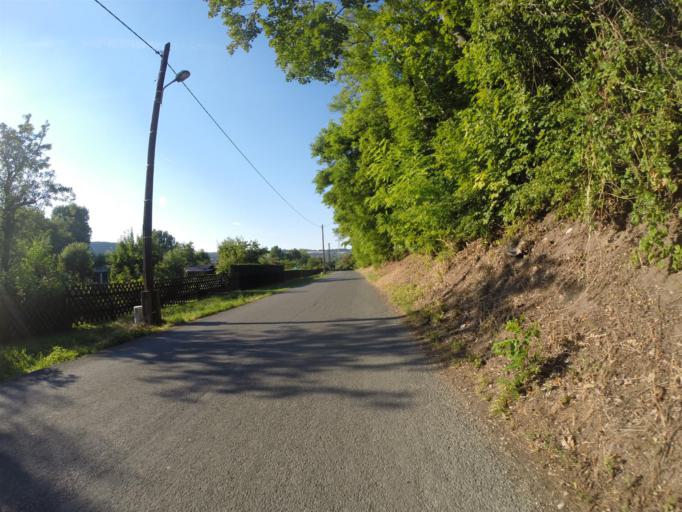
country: DE
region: Thuringia
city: Jena
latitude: 50.9370
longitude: 11.6094
